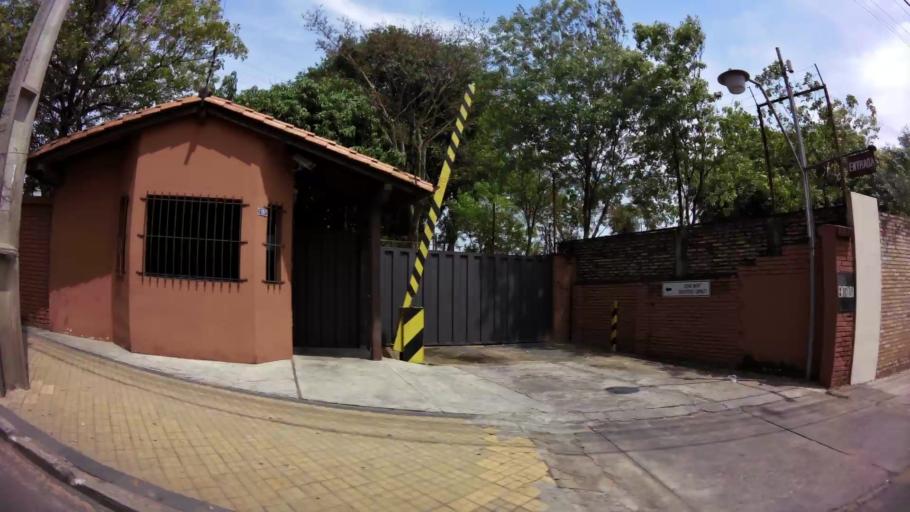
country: PY
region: Asuncion
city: Asuncion
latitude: -25.2780
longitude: -57.5863
